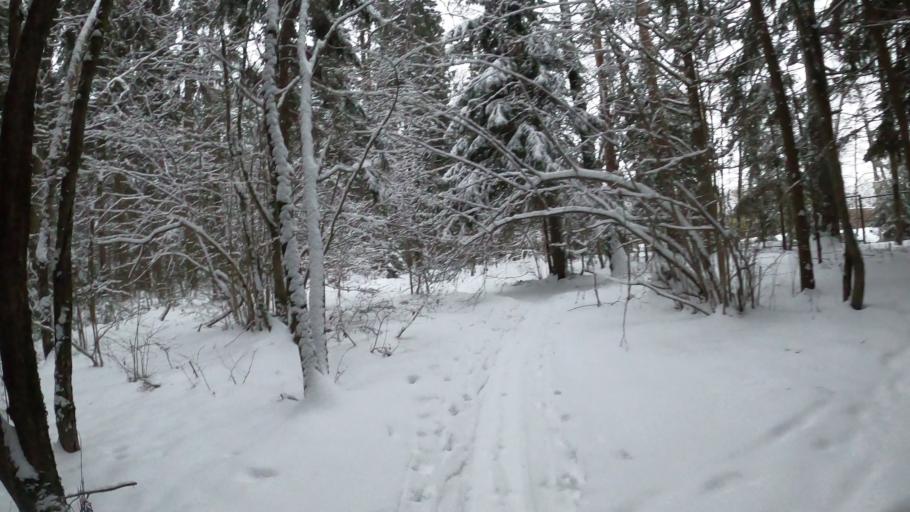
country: RU
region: Moskovskaya
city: Firsanovka
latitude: 55.9144
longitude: 37.2038
